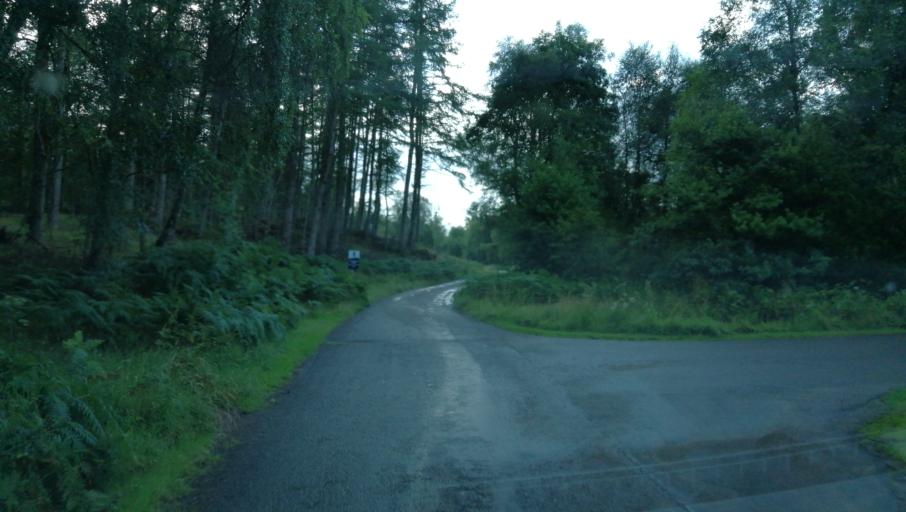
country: GB
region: Scotland
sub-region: Highland
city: Spean Bridge
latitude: 57.0691
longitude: -4.8240
